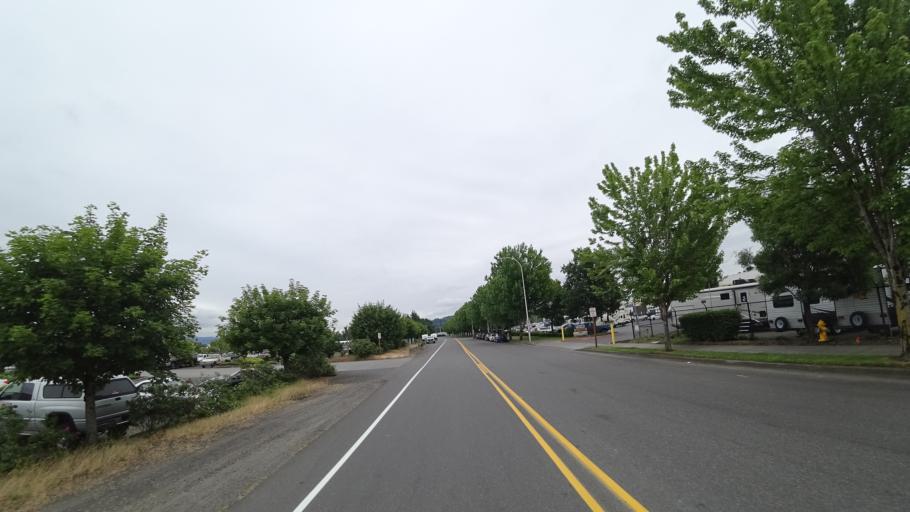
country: US
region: Oregon
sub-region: Multnomah County
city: Wood Village
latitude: 45.5426
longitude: -122.4163
